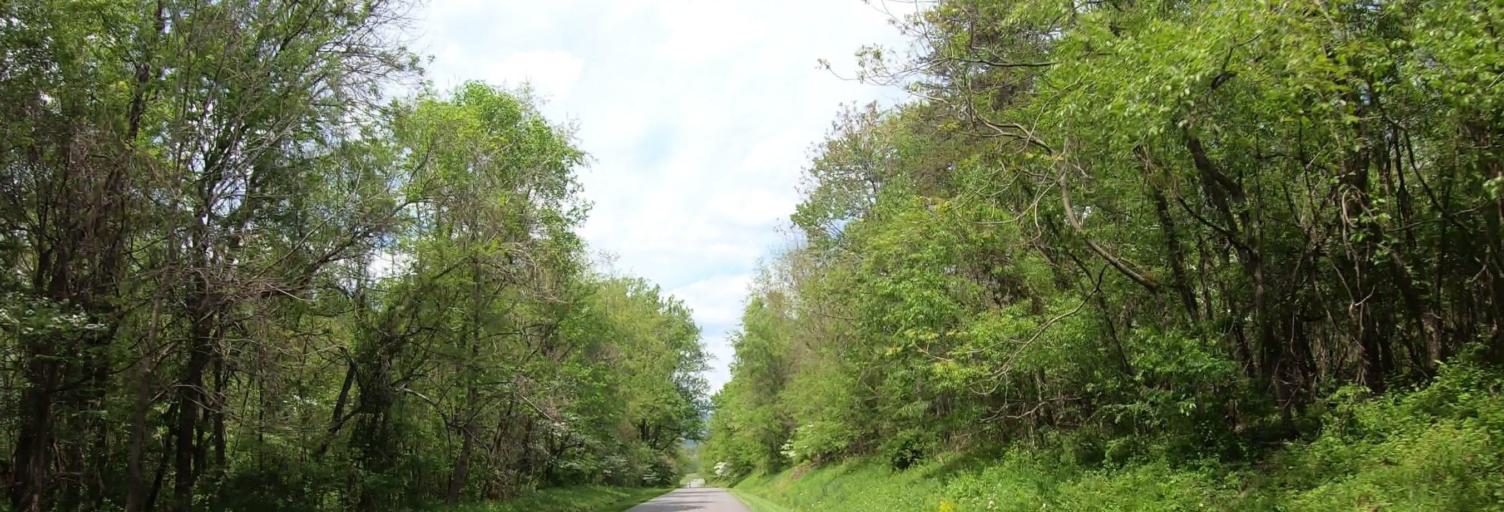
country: US
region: Virginia
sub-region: Botetourt County
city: Laymantown
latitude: 37.3205
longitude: -79.8577
